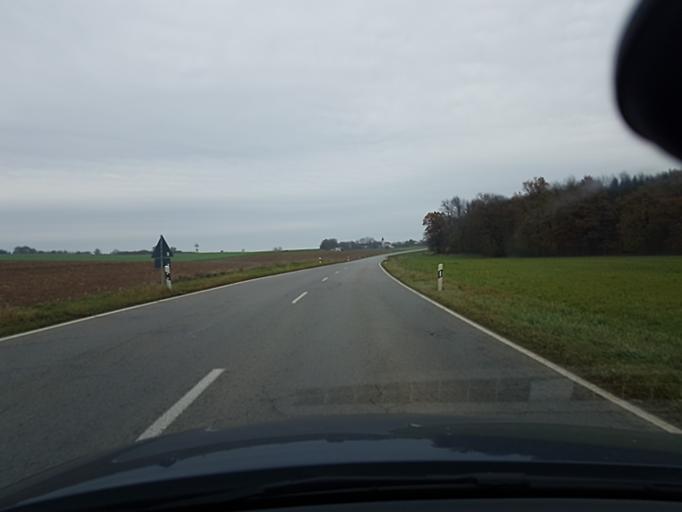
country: DE
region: Bavaria
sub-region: Upper Palatinate
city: Pfakofen
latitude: 48.8681
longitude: 12.1867
